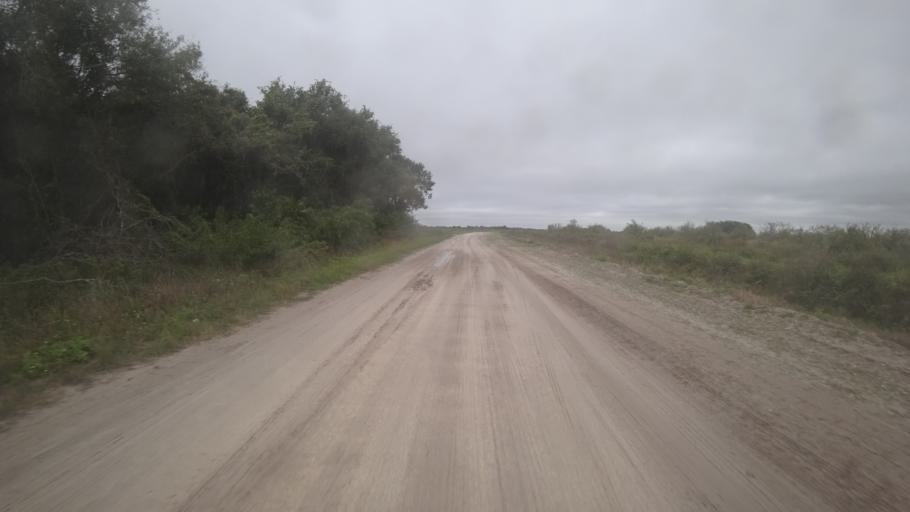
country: US
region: Florida
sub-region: Hillsborough County
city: Wimauma
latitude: 27.5778
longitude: -82.3152
